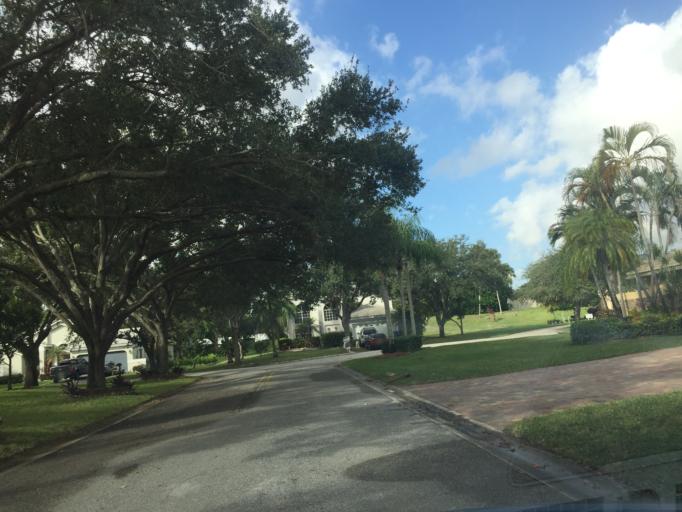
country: US
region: Florida
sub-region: Broward County
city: Tamarac
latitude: 26.2321
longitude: -80.2517
